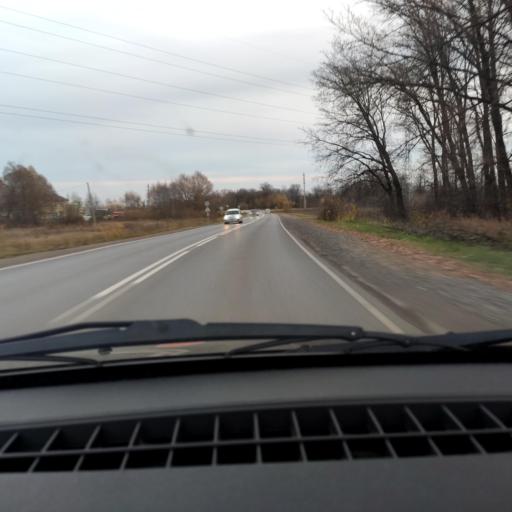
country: RU
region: Bashkortostan
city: Mikhaylovka
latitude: 54.8063
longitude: 55.8224
